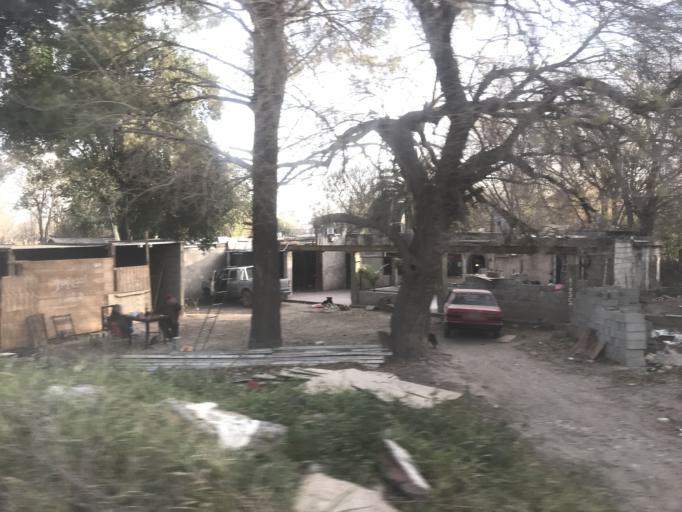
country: AR
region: Cordoba
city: Malvinas Argentinas
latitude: -31.4641
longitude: -64.1041
